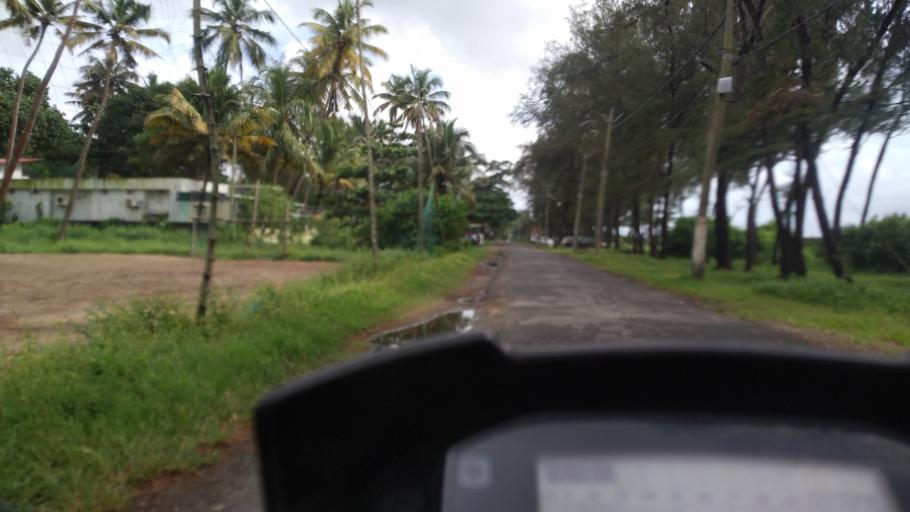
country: IN
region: Kerala
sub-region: Thrissur District
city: Kodungallur
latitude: 10.1530
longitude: 76.1747
